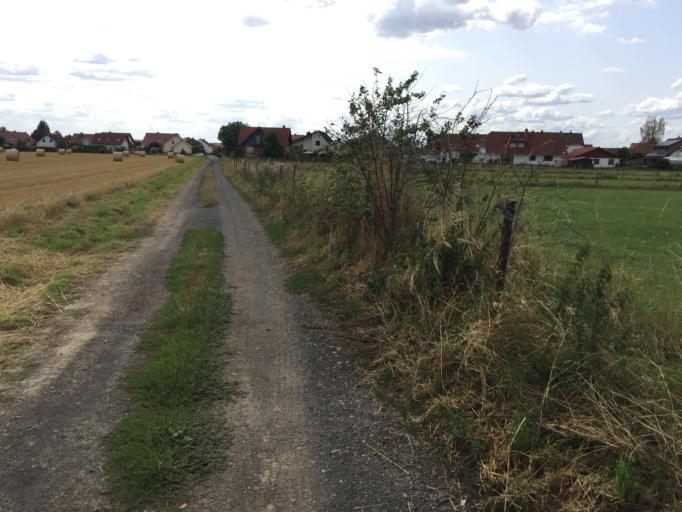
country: DE
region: Hesse
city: Schwalmstadt
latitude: 50.9122
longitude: 9.2602
